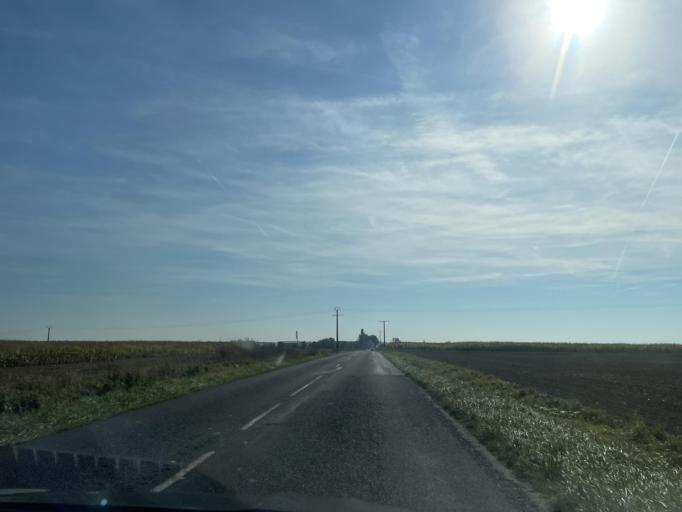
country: FR
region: Ile-de-France
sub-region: Departement de Seine-et-Marne
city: Sammeron
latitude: 48.8818
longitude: 3.0724
